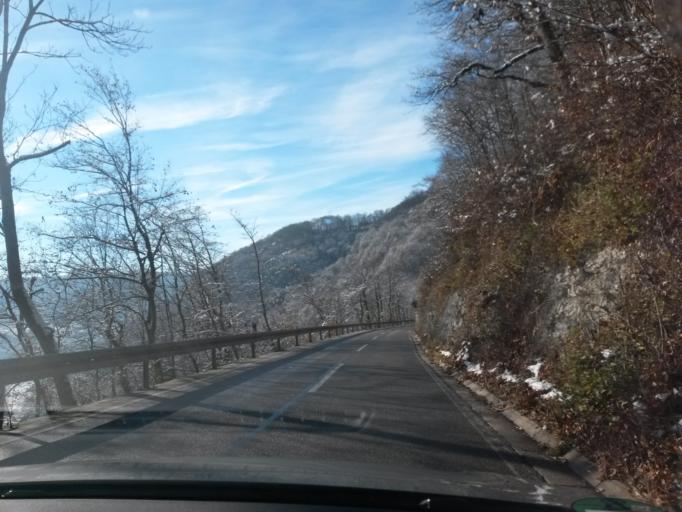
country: DE
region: Baden-Wuerttemberg
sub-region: Regierungsbezirk Stuttgart
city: Bad Uberkingen
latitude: 48.6166
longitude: 9.8025
